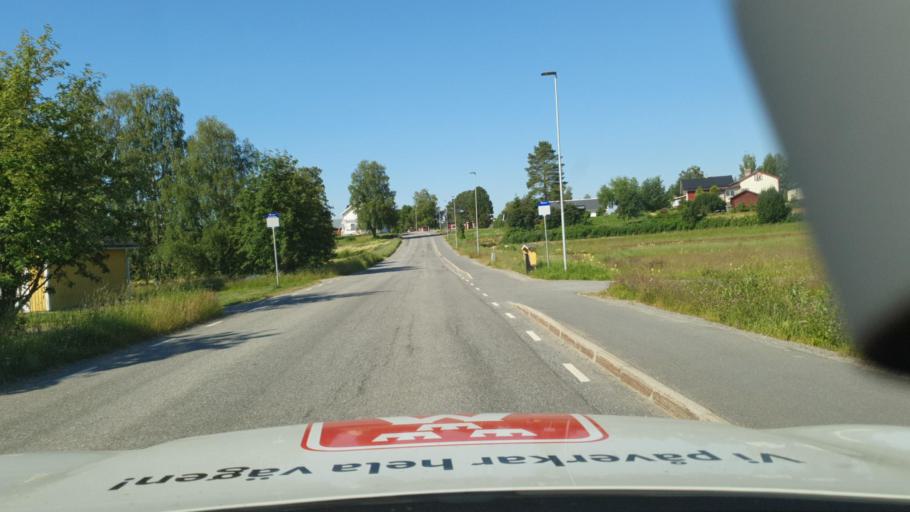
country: SE
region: Vaesterbotten
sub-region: Skelleftea Kommun
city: Viken
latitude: 64.7443
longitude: 20.7521
